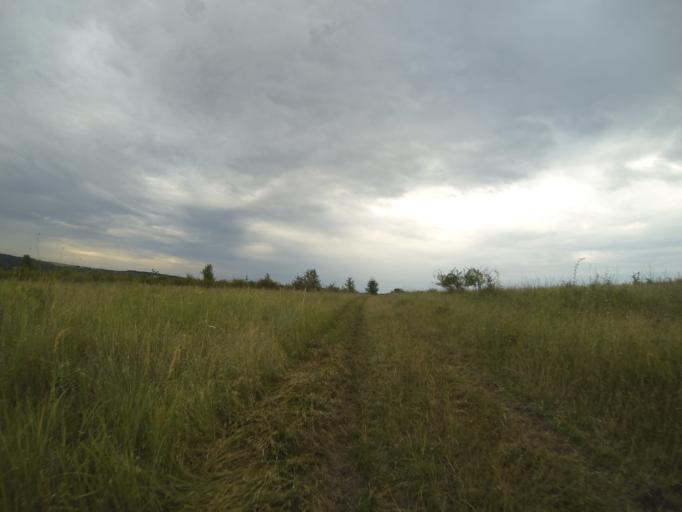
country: RO
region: Dolj
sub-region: Comuna Filiasi
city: Fratostita
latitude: 44.5711
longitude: 23.6204
